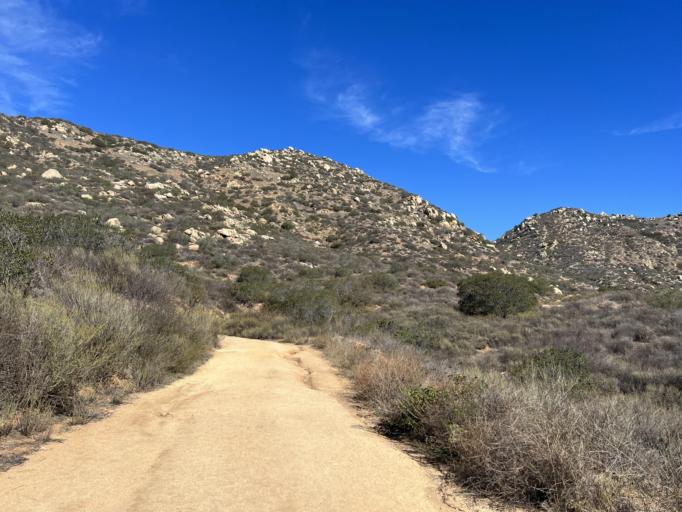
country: US
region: California
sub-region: San Diego County
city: Poway
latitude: 33.0181
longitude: -117.0049
